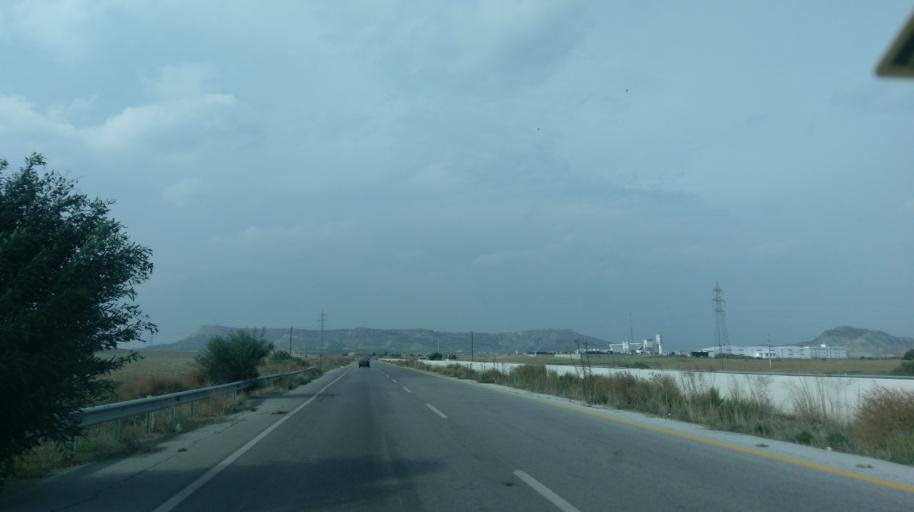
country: CY
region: Lefkosia
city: Mammari
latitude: 35.2207
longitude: 33.1648
